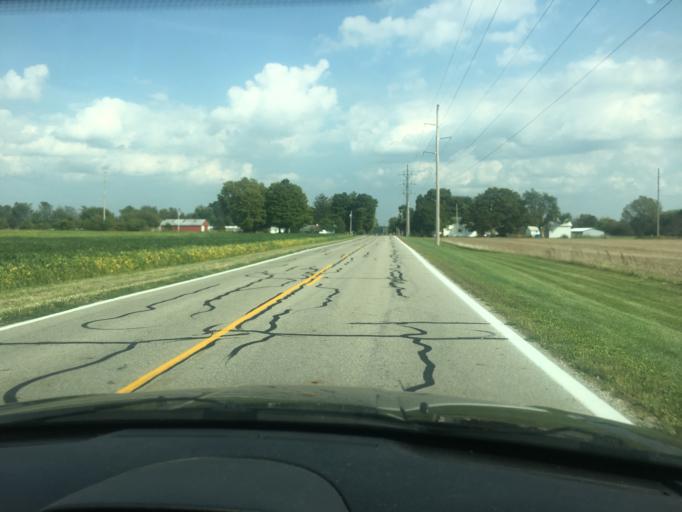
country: US
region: Ohio
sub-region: Champaign County
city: Urbana
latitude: 40.1279
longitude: -83.7797
